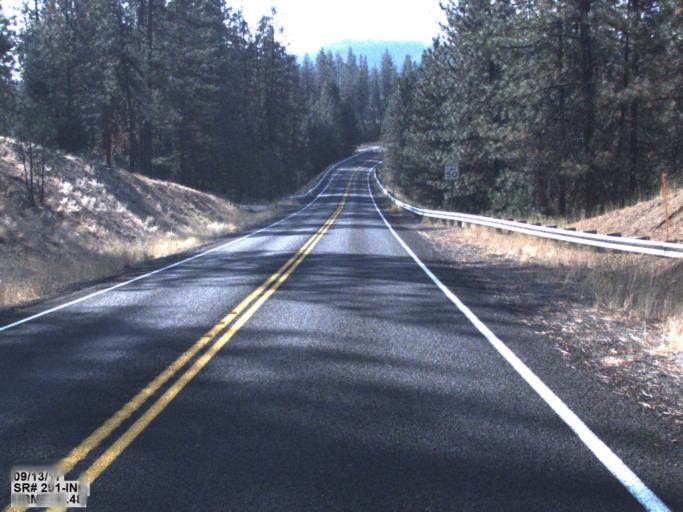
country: US
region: Washington
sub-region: Spokane County
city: Deer Park
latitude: 47.8722
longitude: -117.7074
